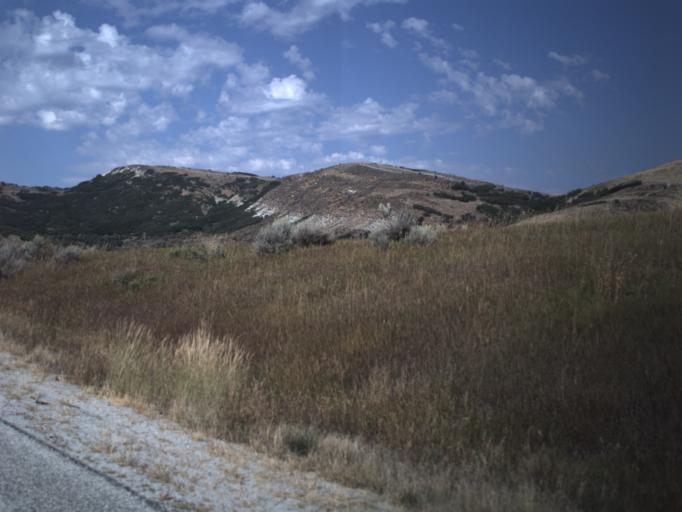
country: US
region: Utah
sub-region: Morgan County
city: Mountain Green
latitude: 41.1618
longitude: -111.7981
